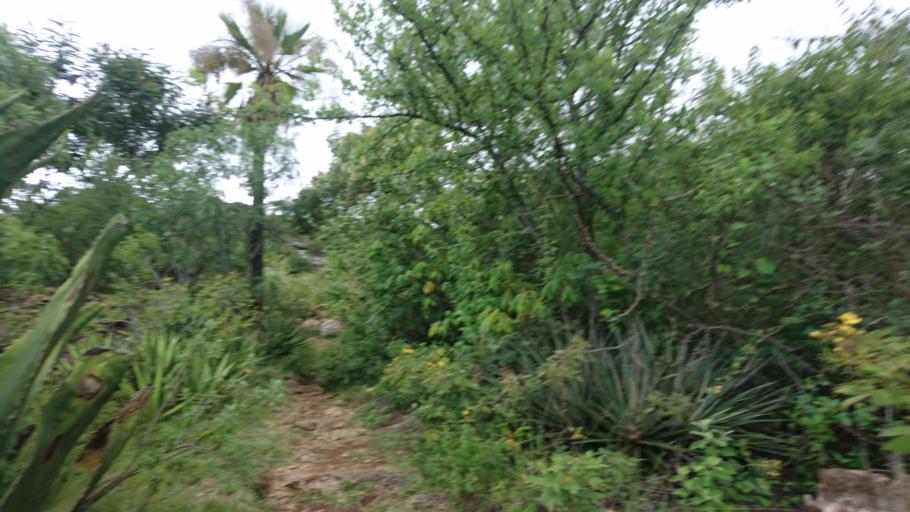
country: MX
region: Oaxaca
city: San Lorenzo Albarradas
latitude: 16.8689
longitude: -96.2740
